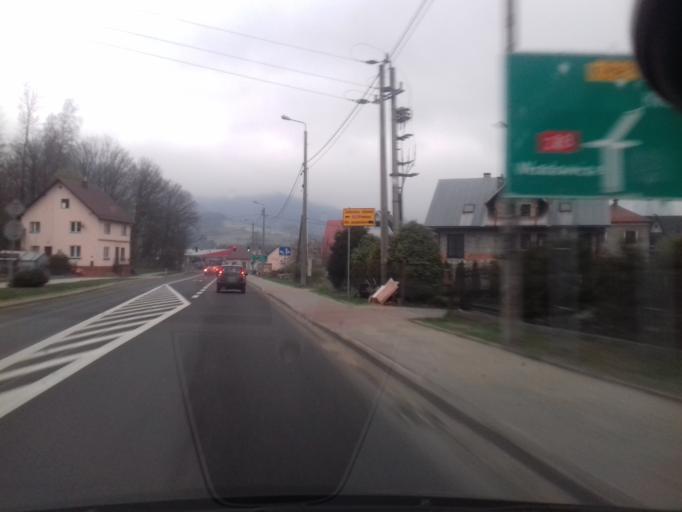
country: PL
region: Lesser Poland Voivodeship
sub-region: Powiat limanowski
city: Mszana Dolna
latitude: 49.6752
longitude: 20.0668
